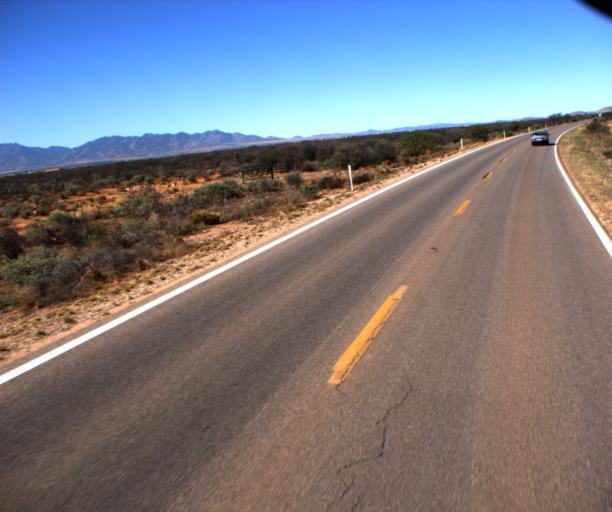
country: US
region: Arizona
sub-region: Cochise County
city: Huachuca City
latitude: 31.6965
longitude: -110.3056
